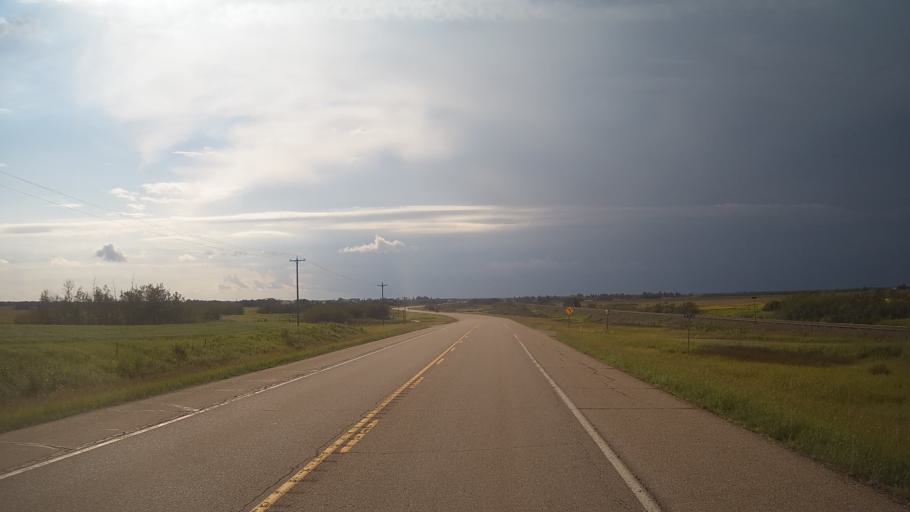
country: CA
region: Alberta
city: Viking
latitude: 53.1625
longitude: -112.0102
